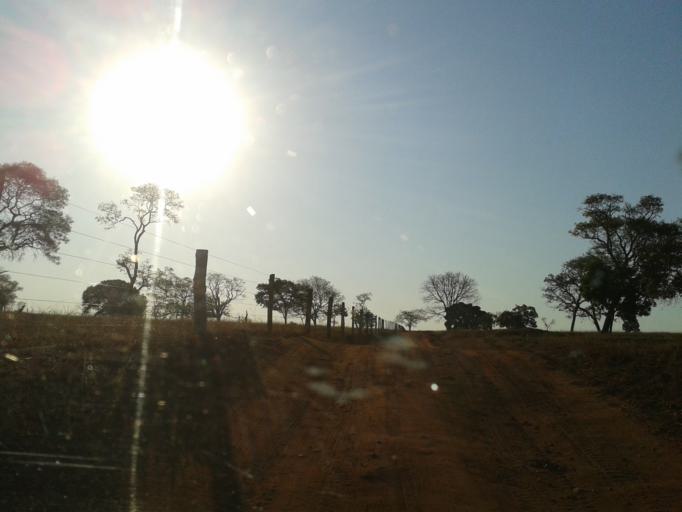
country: BR
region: Minas Gerais
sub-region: Ituiutaba
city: Ituiutaba
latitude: -19.2466
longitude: -49.5852
